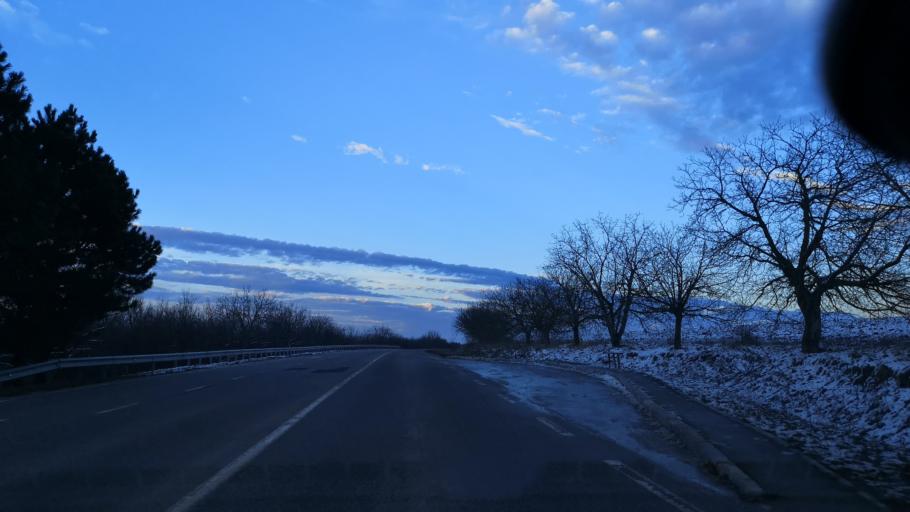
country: MD
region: Orhei
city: Orhei
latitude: 47.5521
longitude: 28.7942
